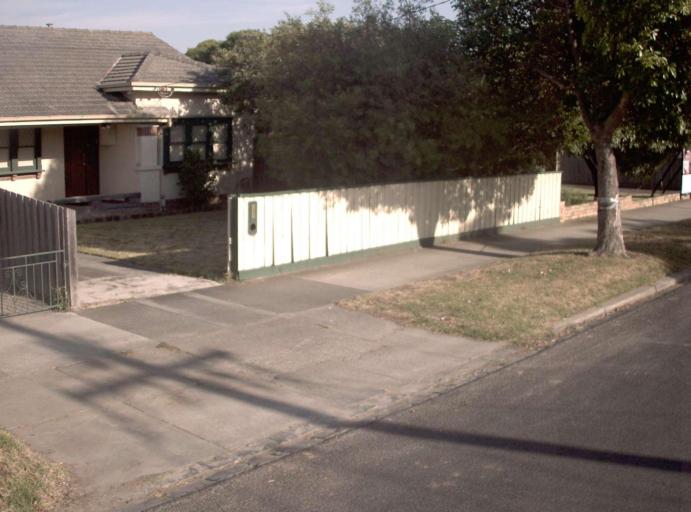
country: AU
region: Victoria
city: Murrumbeena
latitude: -37.9002
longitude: 145.0645
